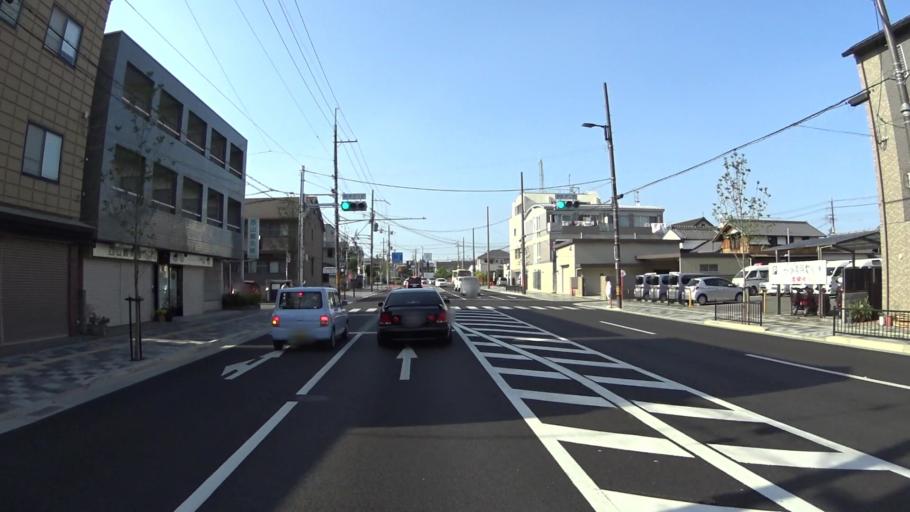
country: JP
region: Kyoto
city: Muko
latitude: 34.9244
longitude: 135.6981
